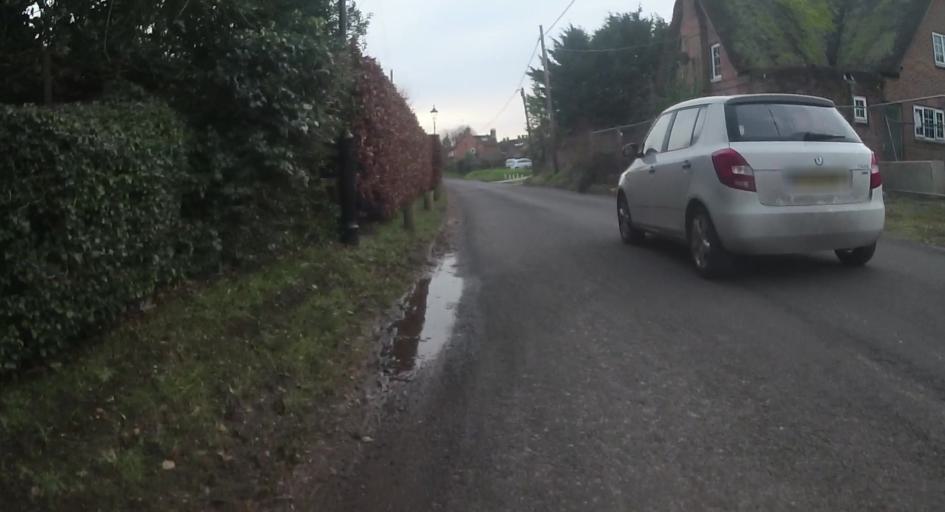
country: GB
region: England
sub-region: Hampshire
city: Overton
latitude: 51.2143
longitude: -1.3752
